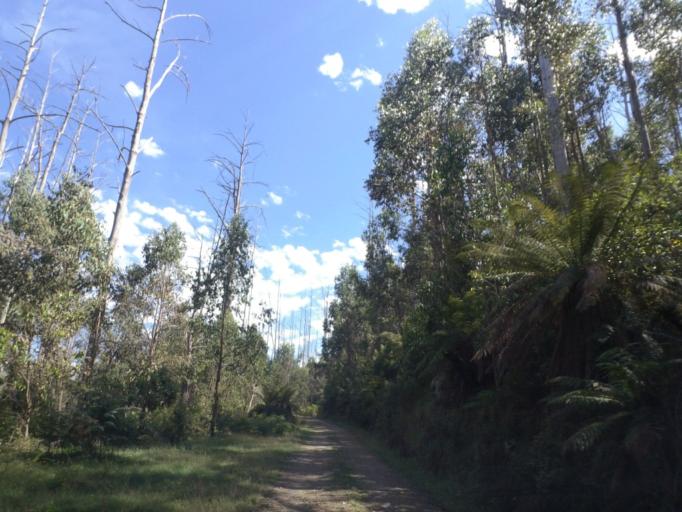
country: AU
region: Victoria
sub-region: Yarra Ranges
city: Millgrove
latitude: -37.4966
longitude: 145.8469
